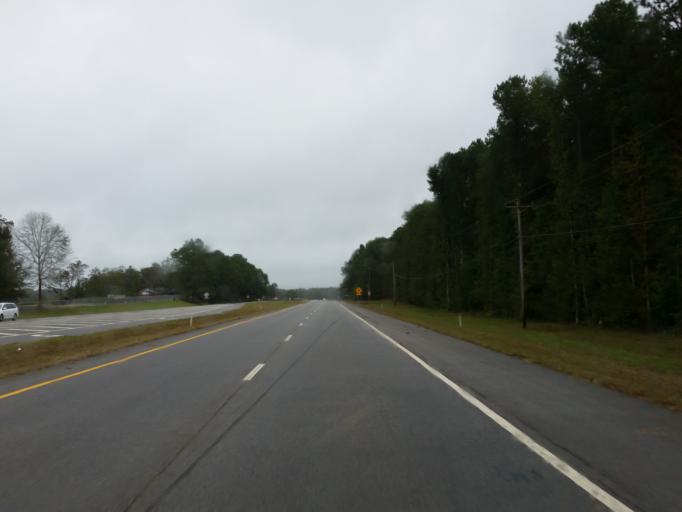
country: US
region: Georgia
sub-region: Lamar County
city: Barnesville
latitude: 33.1051
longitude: -84.1915
